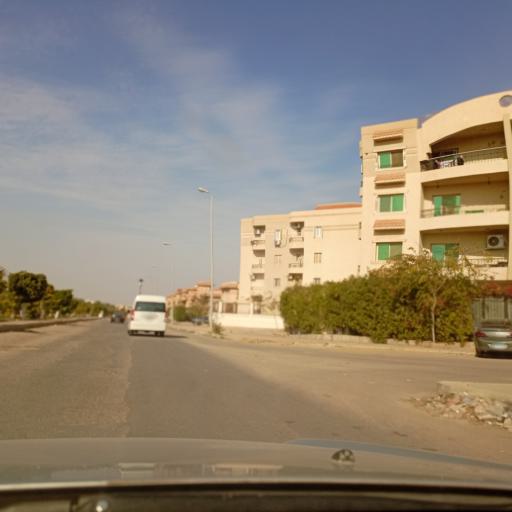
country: EG
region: Muhafazat al Qalyubiyah
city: Al Khankah
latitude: 30.0493
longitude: 31.4853
